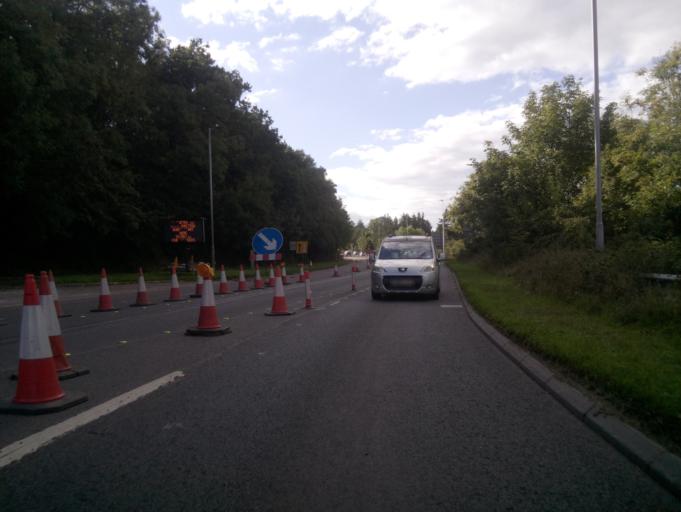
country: GB
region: England
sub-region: Devon
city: Exminster
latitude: 50.6914
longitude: -3.5081
